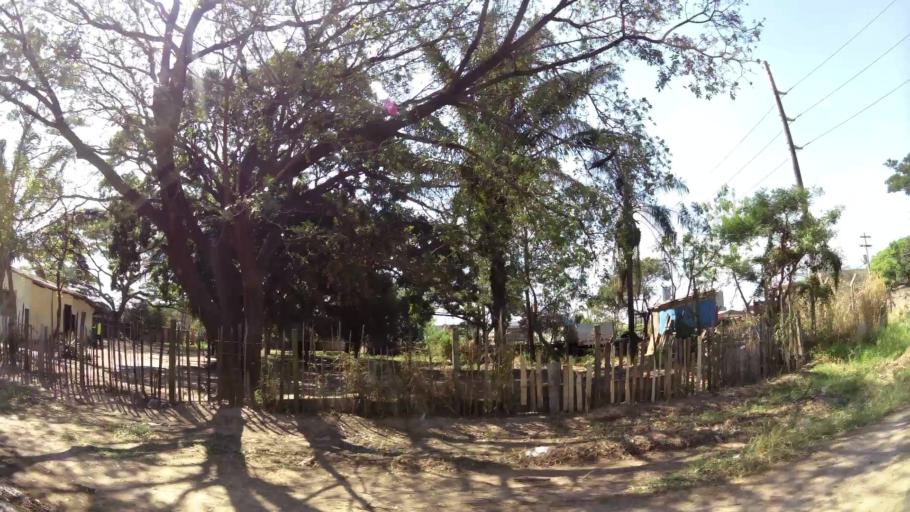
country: BO
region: Santa Cruz
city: Santa Cruz de la Sierra
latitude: -17.7298
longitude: -63.1598
